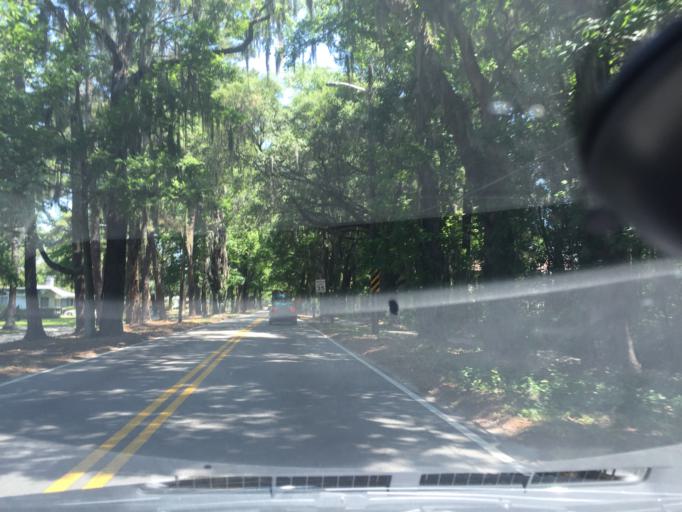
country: US
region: Georgia
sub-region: Chatham County
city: Savannah
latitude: 32.0311
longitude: -81.1101
